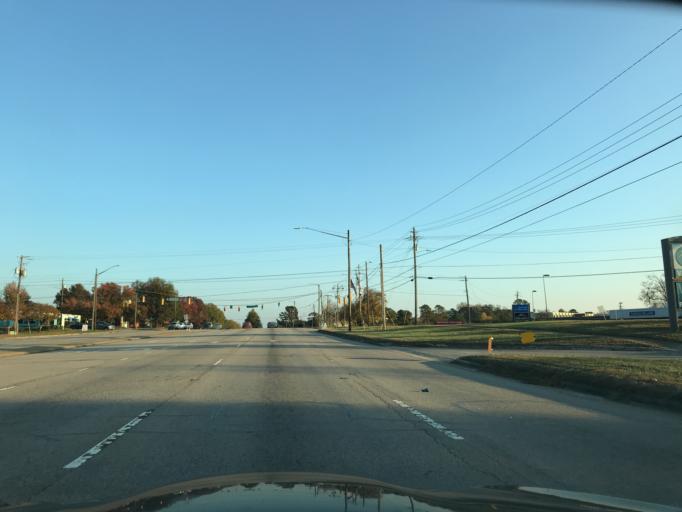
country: US
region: North Carolina
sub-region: Wake County
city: West Raleigh
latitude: 35.8596
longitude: -78.7077
